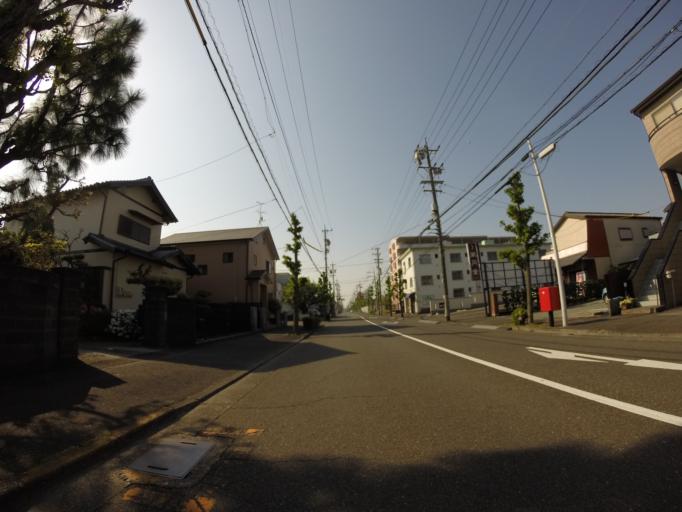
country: JP
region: Shizuoka
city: Shizuoka-shi
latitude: 35.0033
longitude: 138.4878
